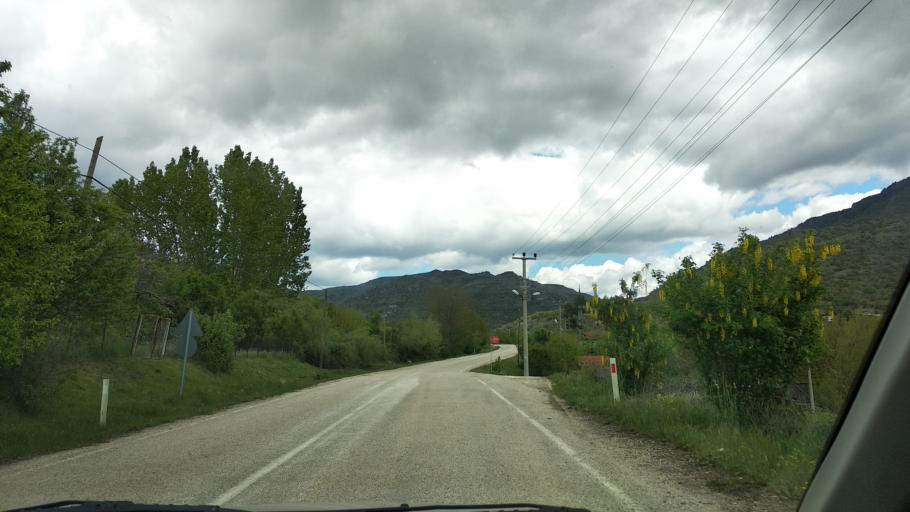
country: TR
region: Bolu
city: Seben
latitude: 40.4181
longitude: 31.5819
